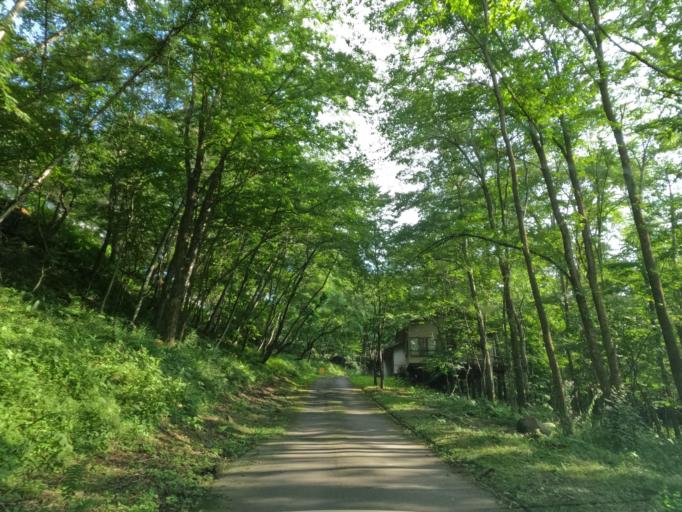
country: JP
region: Nagano
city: Komoro
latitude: 36.4761
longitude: 138.5439
